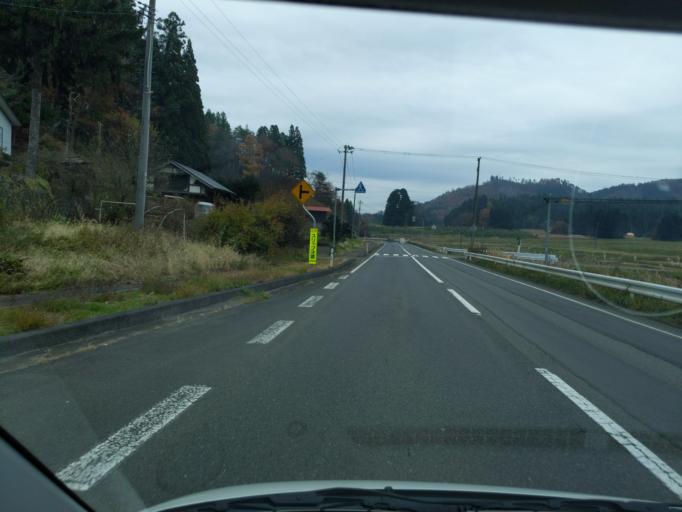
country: JP
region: Iwate
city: Kitakami
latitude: 39.2955
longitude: 141.1866
